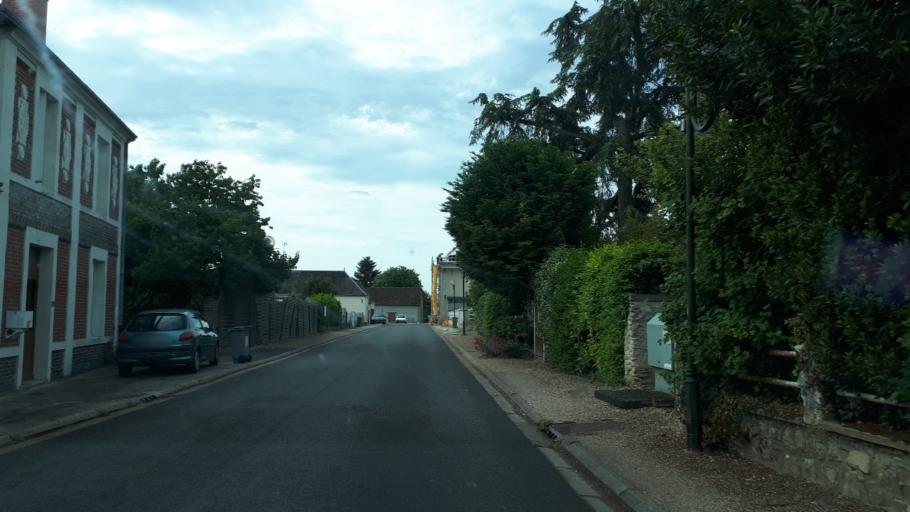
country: FR
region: Centre
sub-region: Departement du Loir-et-Cher
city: Saint-Amand-Longpre
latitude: 47.7230
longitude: 1.0094
